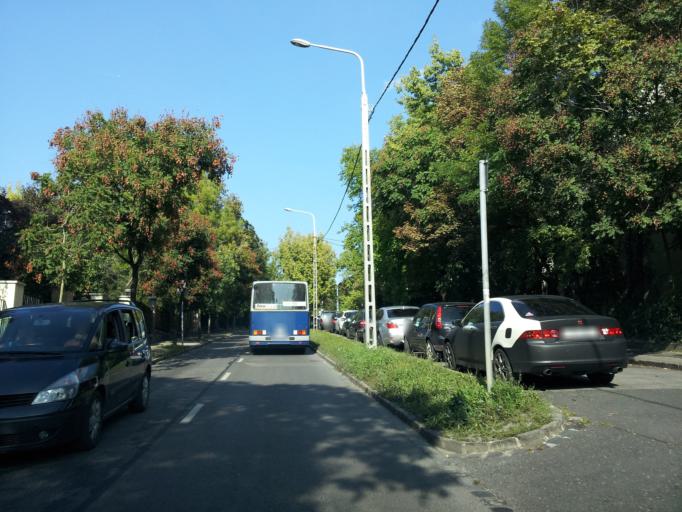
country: HU
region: Budapest
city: Budapest XII. keruelet
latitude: 47.5168
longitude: 19.0046
